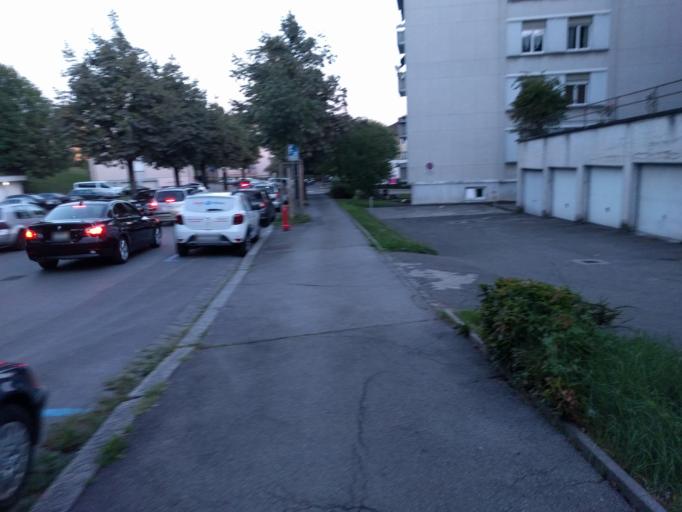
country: CH
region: Vaud
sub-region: Lausanne District
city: Blecherette
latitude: 46.5293
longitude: 6.6075
